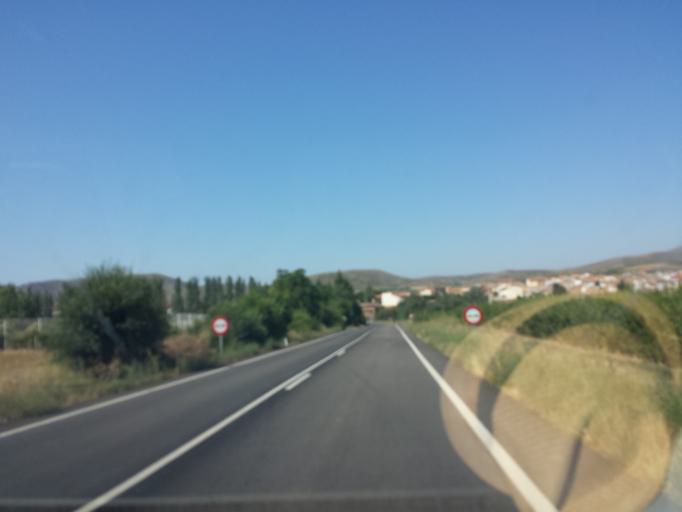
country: ES
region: Aragon
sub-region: Provincia de Zaragoza
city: Munebrega
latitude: 41.2518
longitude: -1.6990
